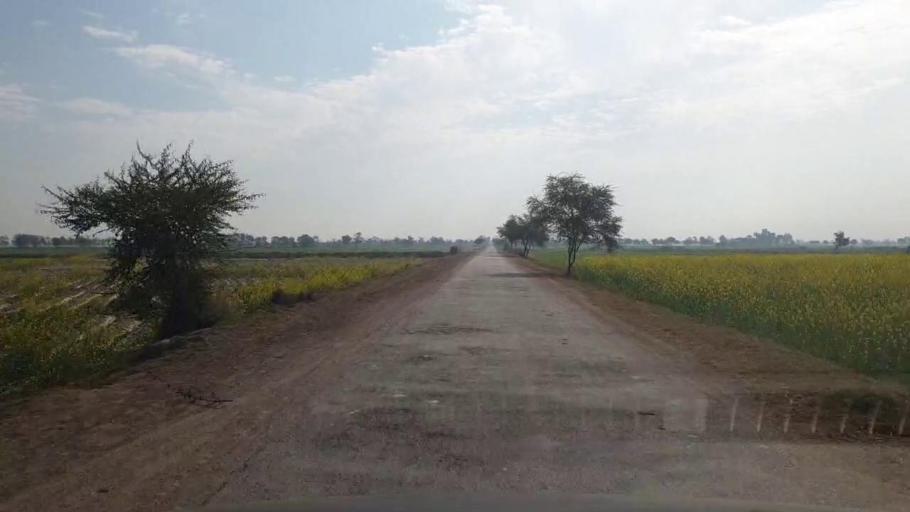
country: PK
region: Sindh
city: Hala
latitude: 25.9977
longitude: 68.4125
